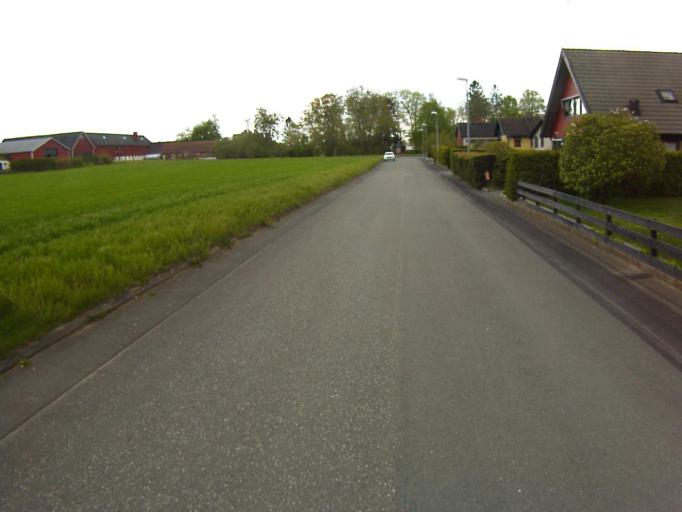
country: SE
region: Skane
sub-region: Kristianstads Kommun
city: Fjalkinge
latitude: 56.0156
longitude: 14.2346
